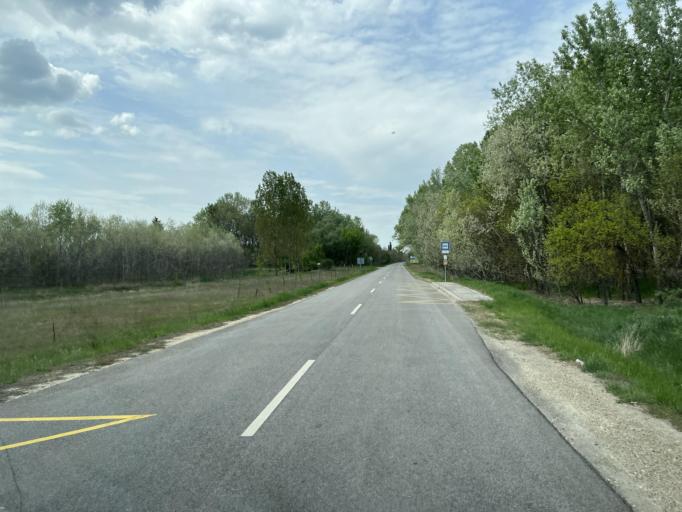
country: HU
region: Pest
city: Csemo
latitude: 47.0997
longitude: 19.6339
